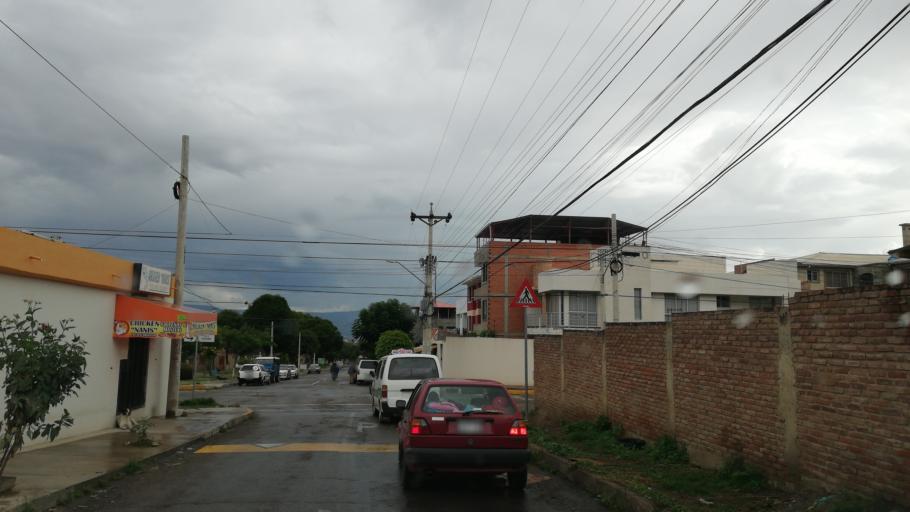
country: BO
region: Cochabamba
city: Cochabamba
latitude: -17.3503
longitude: -66.1801
